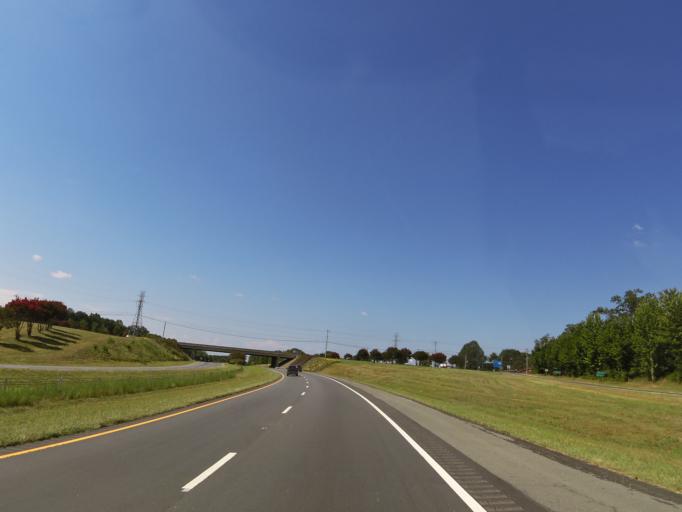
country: US
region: North Carolina
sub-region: Catawba County
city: Maiden
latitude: 35.5261
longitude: -81.2219
